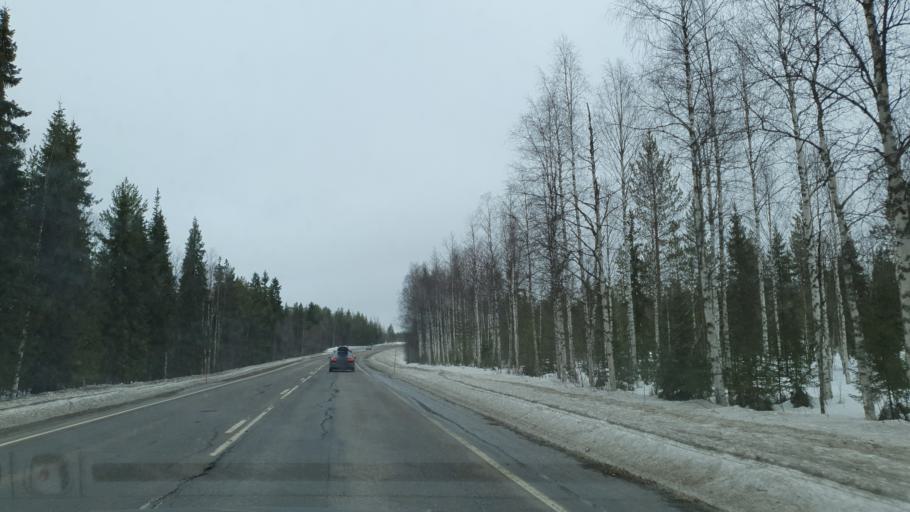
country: FI
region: Lapland
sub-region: Torniolaakso
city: Pello
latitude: 66.8387
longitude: 24.0115
